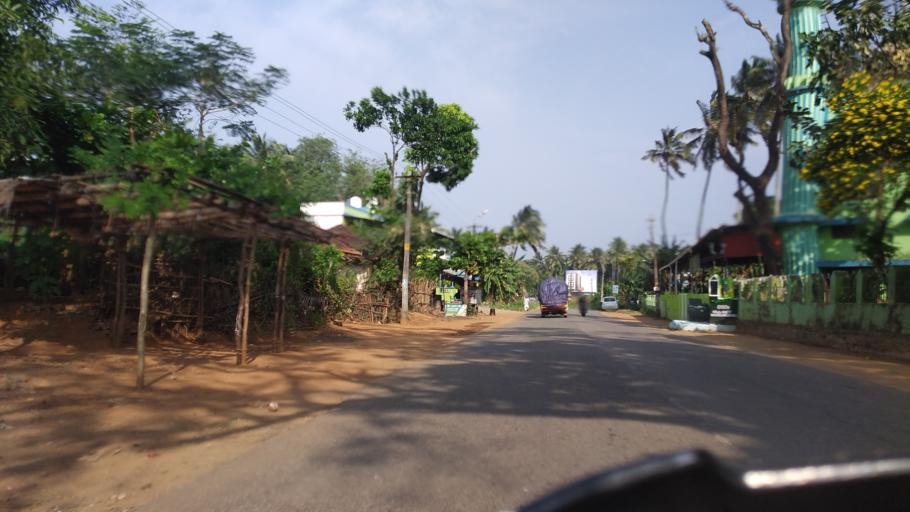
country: IN
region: Kerala
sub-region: Palakkad district
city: Palakkad
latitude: 10.6015
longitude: 76.5381
